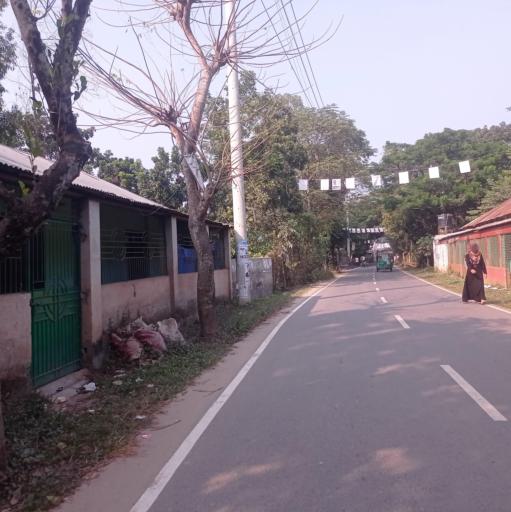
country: BD
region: Dhaka
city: Bhairab Bazar
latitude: 24.0379
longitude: 90.8320
